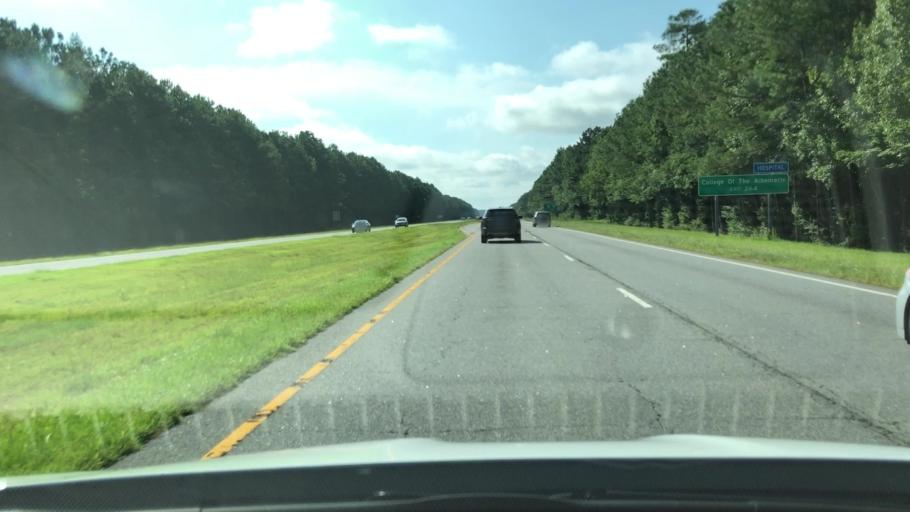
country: US
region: North Carolina
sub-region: Pasquotank County
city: Elizabeth City
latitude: 36.3905
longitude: -76.3220
